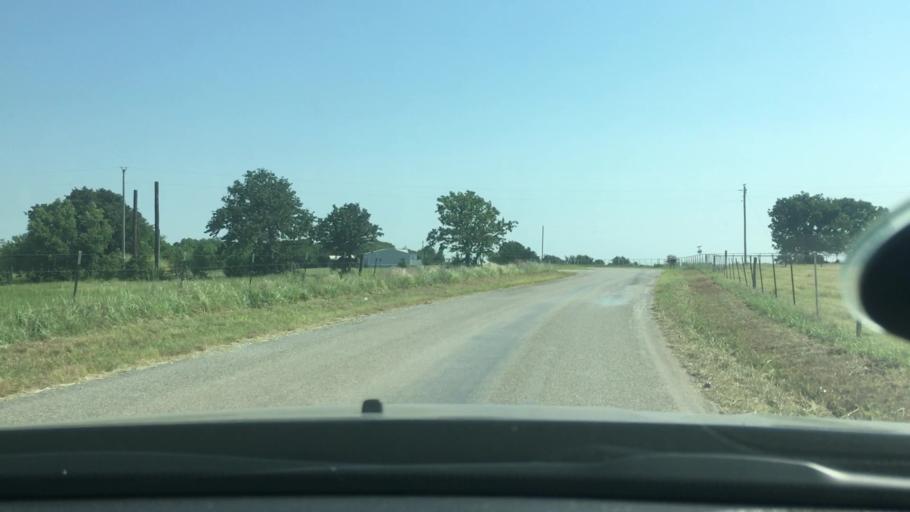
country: US
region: Oklahoma
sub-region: Garvin County
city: Lindsay
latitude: 34.7751
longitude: -97.6115
